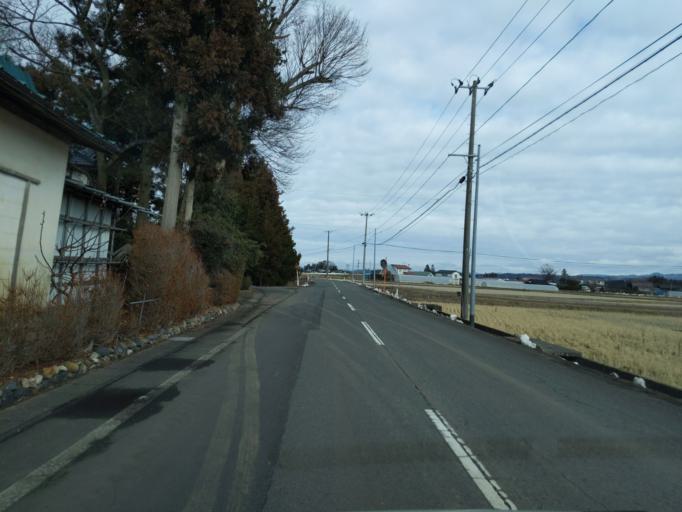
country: JP
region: Iwate
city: Mizusawa
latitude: 39.0780
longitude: 141.1650
